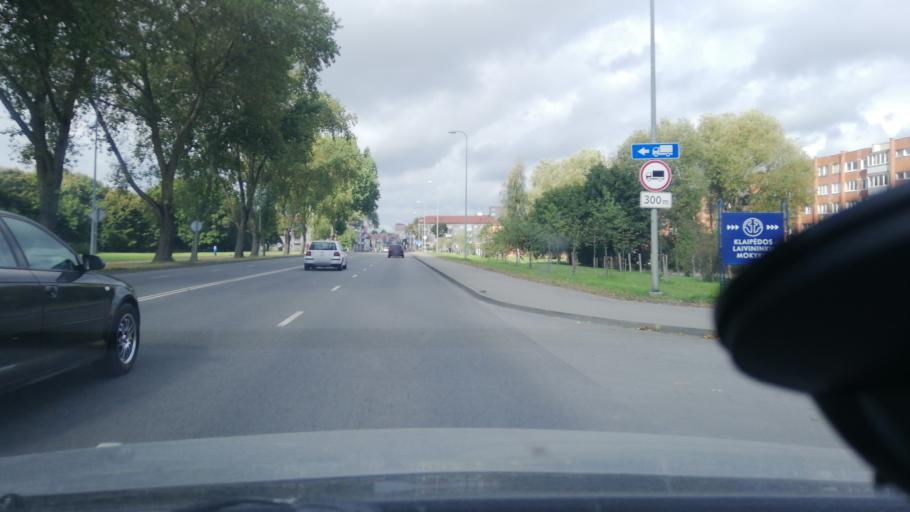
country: LT
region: Klaipedos apskritis
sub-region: Klaipeda
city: Klaipeda
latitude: 55.6734
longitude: 21.1566
